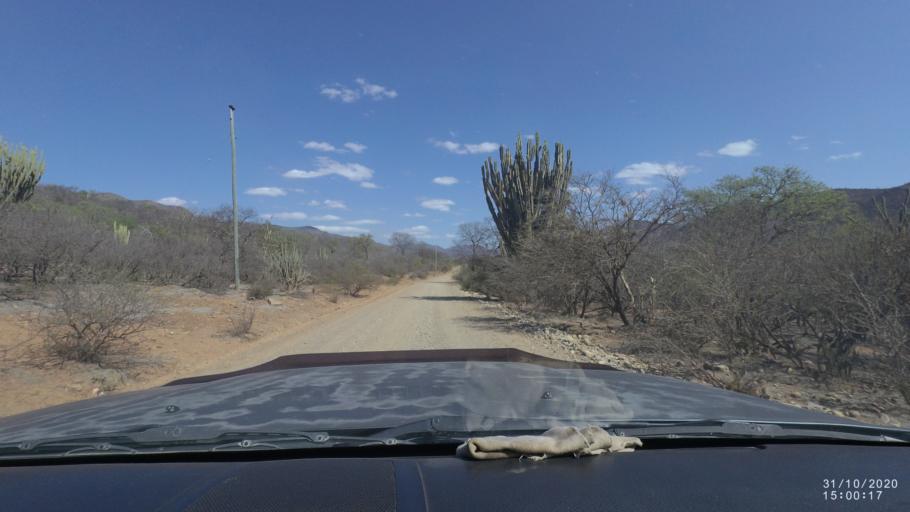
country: BO
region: Cochabamba
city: Aiquile
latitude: -18.2563
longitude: -64.8259
